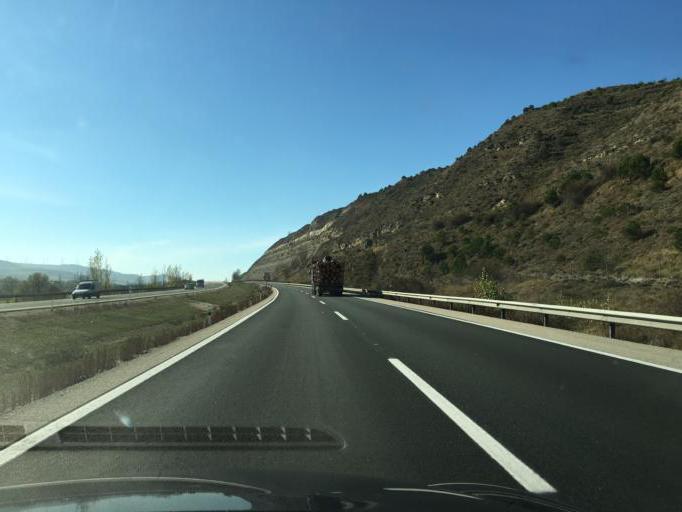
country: ES
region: Castille and Leon
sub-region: Provincia de Burgos
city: Reinoso
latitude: 42.4967
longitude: -3.3678
